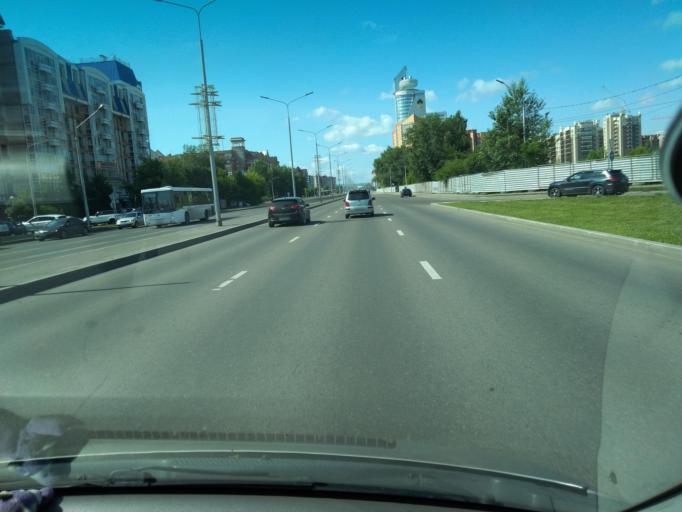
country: RU
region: Krasnoyarskiy
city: Krasnoyarsk
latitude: 56.0466
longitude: 92.9151
